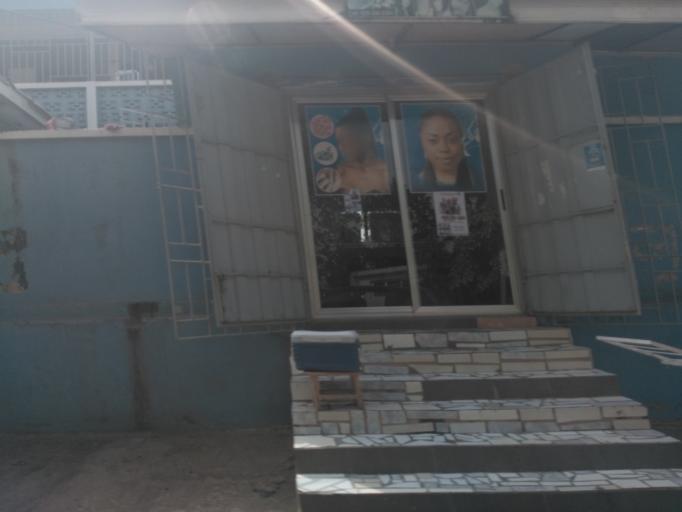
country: GH
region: Ashanti
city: Kumasi
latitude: 6.6775
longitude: -1.6031
